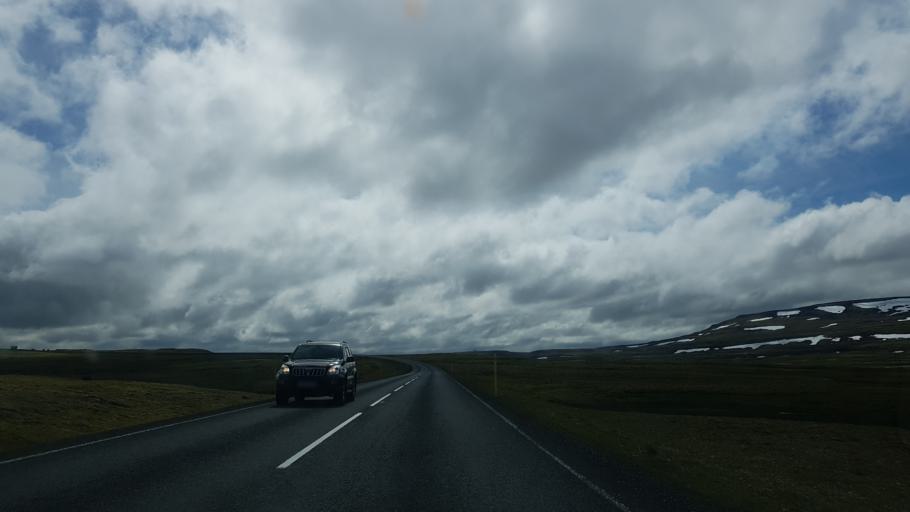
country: IS
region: West
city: Borgarnes
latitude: 65.0032
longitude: -21.0669
